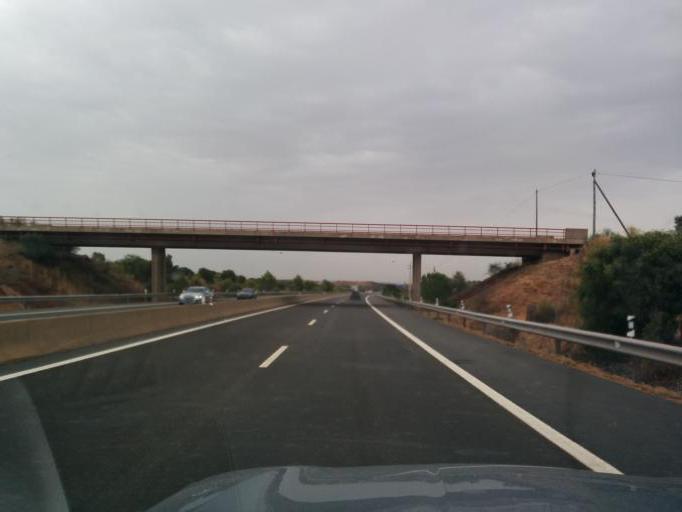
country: PT
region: Faro
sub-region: Vila Real de Santo Antonio
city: Monte Gordo
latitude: 37.1994
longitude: -7.5197
